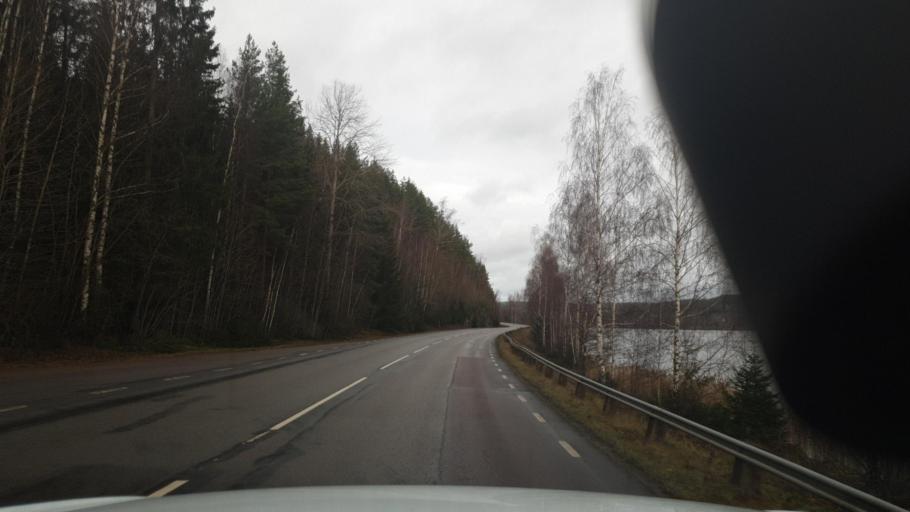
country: SE
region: Vaermland
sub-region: Arvika Kommun
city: Arvika
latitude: 59.7060
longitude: 12.6356
